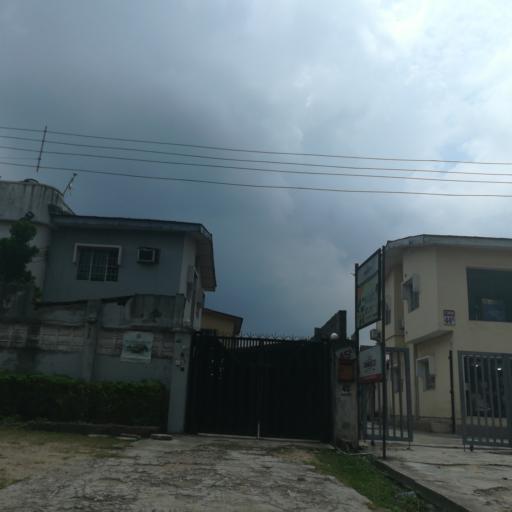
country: NG
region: Lagos
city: Ojota
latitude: 6.5790
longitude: 3.3872
